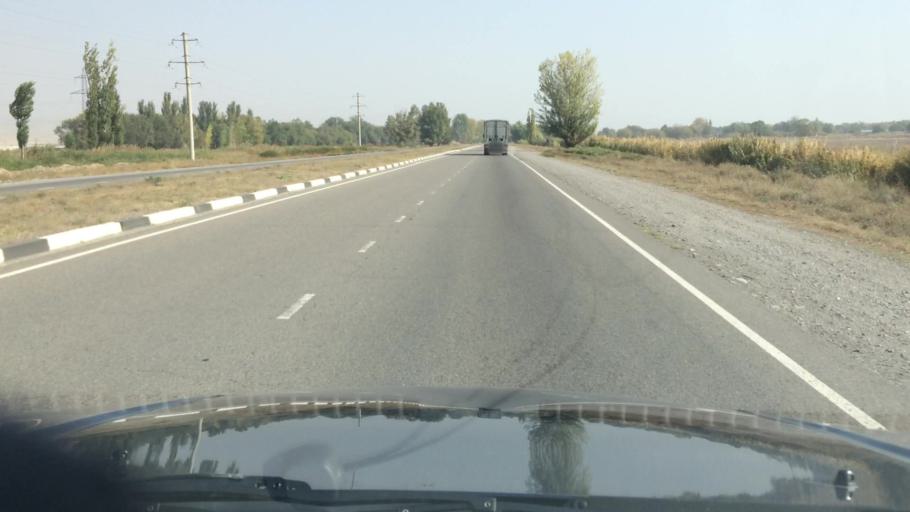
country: KG
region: Chuy
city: Kant
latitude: 42.9692
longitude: 74.8475
